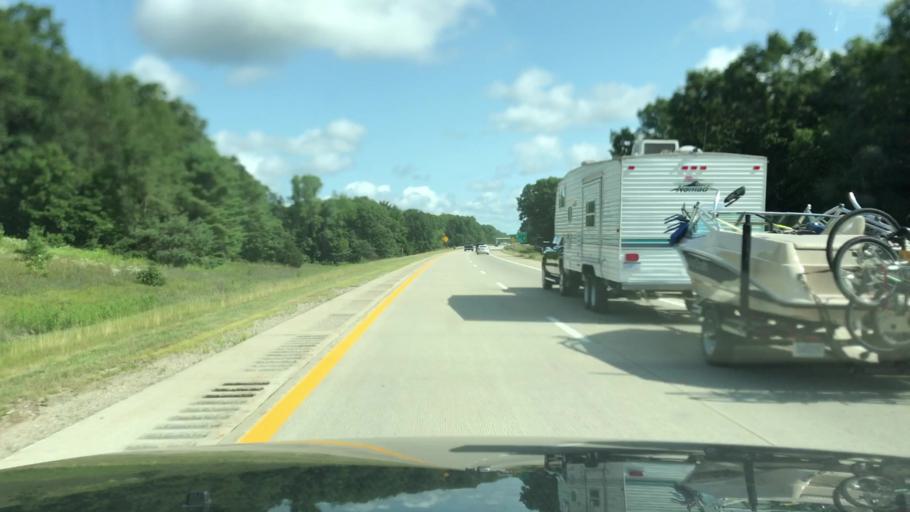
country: US
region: Michigan
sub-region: Montcalm County
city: Howard City
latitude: 43.3858
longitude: -85.5172
